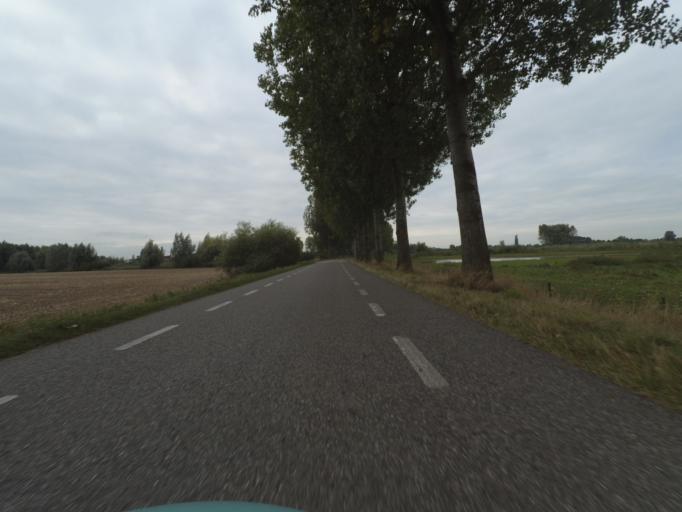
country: NL
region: Gelderland
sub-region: Gemeente Culemborg
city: Culemborg
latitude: 51.9605
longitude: 5.2812
